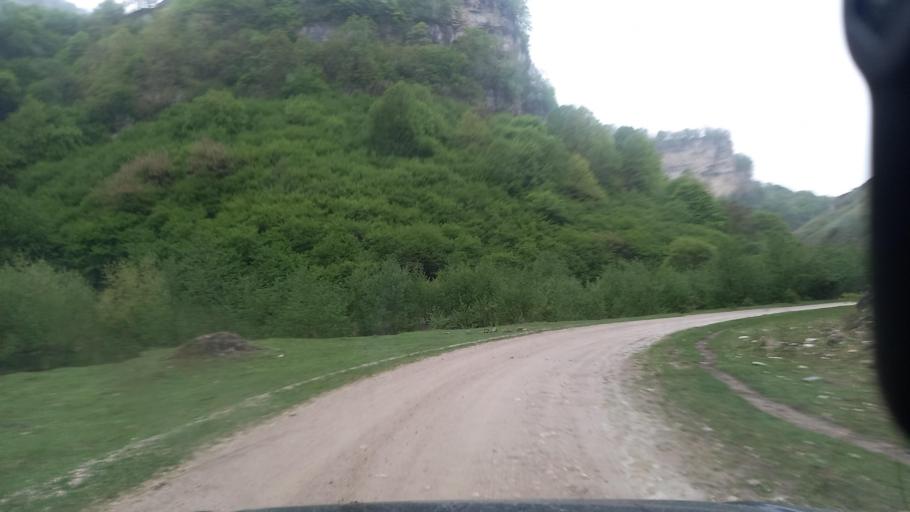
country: RU
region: Kabardino-Balkariya
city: Gundelen
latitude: 43.5955
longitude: 43.1416
